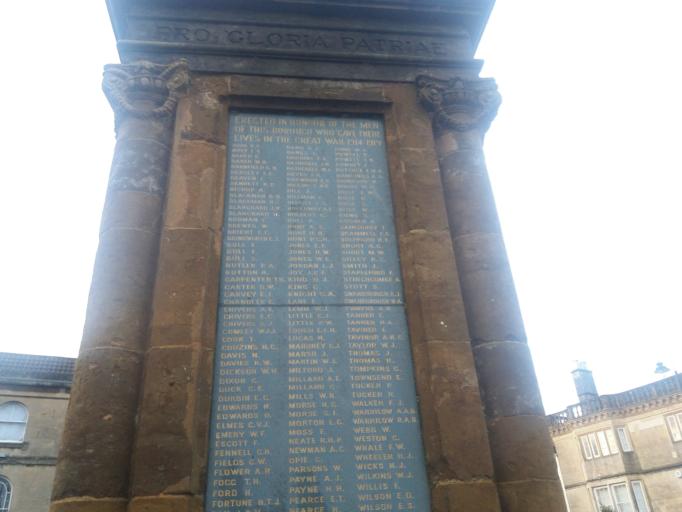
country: GB
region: England
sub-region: Wiltshire
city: Chippenham
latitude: 51.4577
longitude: -2.1135
